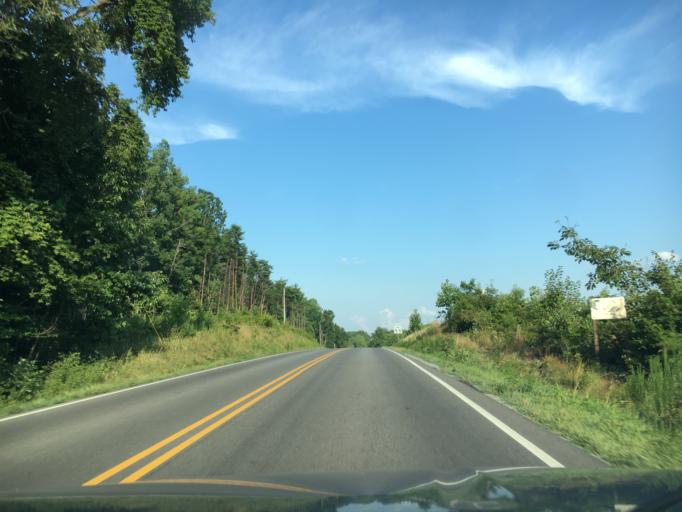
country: US
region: Virginia
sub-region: Franklin County
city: Union Hall
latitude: 36.9748
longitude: -79.6118
